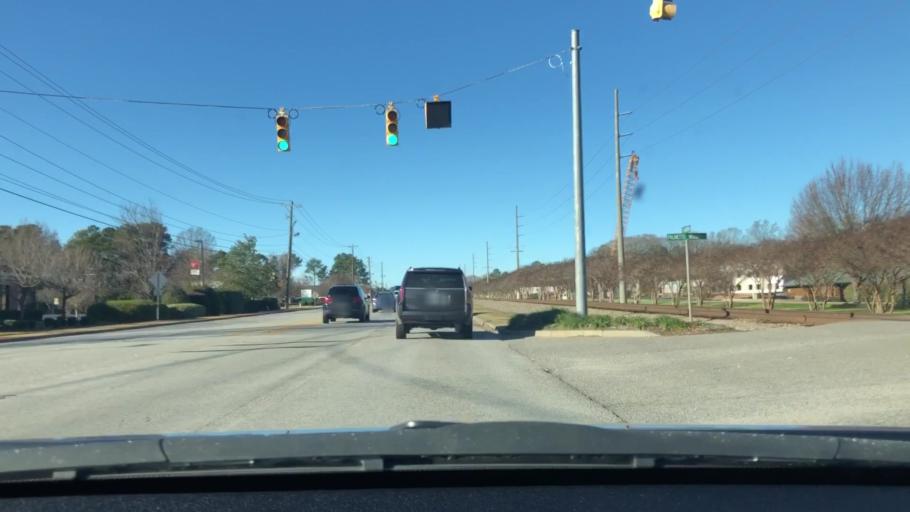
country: US
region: South Carolina
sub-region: Lexington County
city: Irmo
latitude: 34.0782
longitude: -81.1789
